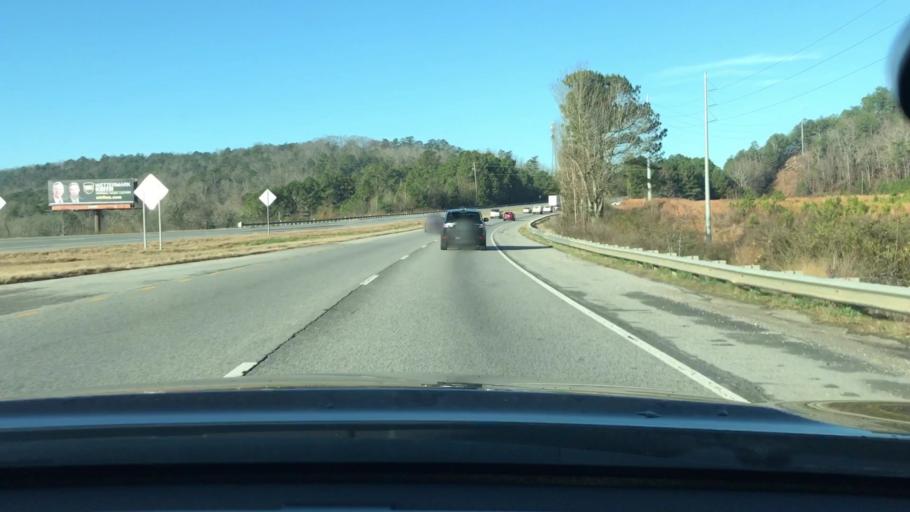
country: US
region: Alabama
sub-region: Shelby County
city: Chelsea
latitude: 33.3478
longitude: -86.6368
